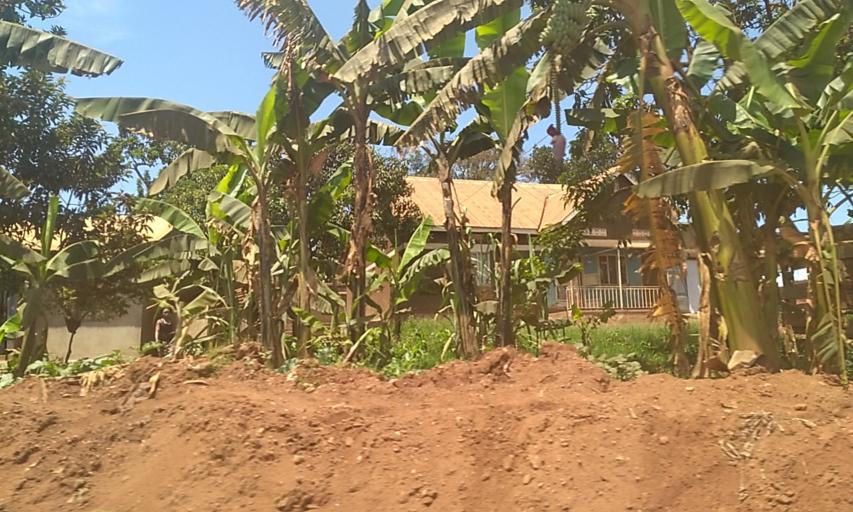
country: UG
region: Central Region
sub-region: Wakiso District
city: Wakiso
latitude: 0.4004
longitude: 32.4847
